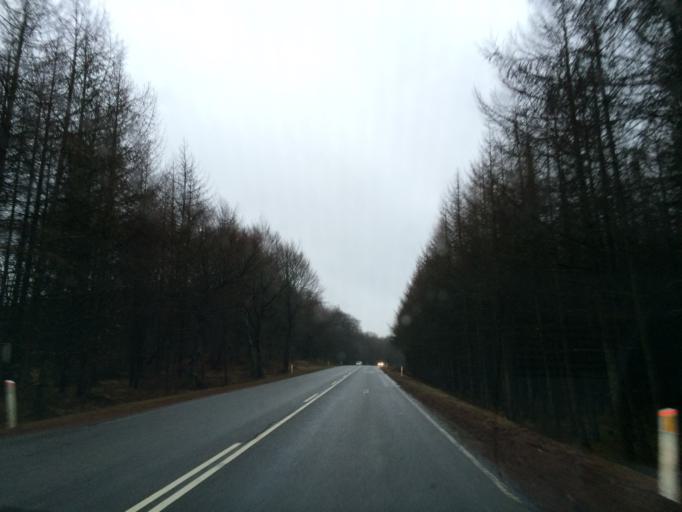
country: DK
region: North Denmark
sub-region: Mariagerfjord Kommune
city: Arden
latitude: 56.7953
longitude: 9.8205
